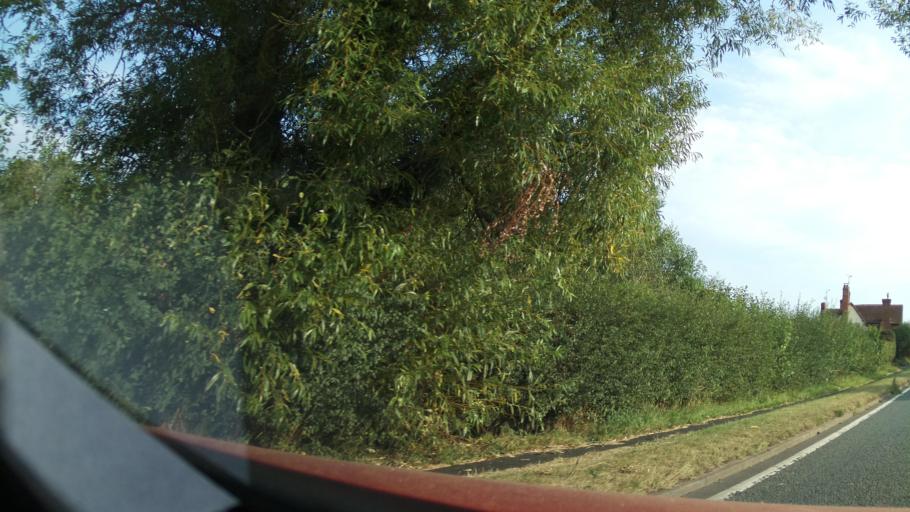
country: GB
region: England
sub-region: Warwickshire
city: Studley
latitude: 52.2543
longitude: -1.8882
